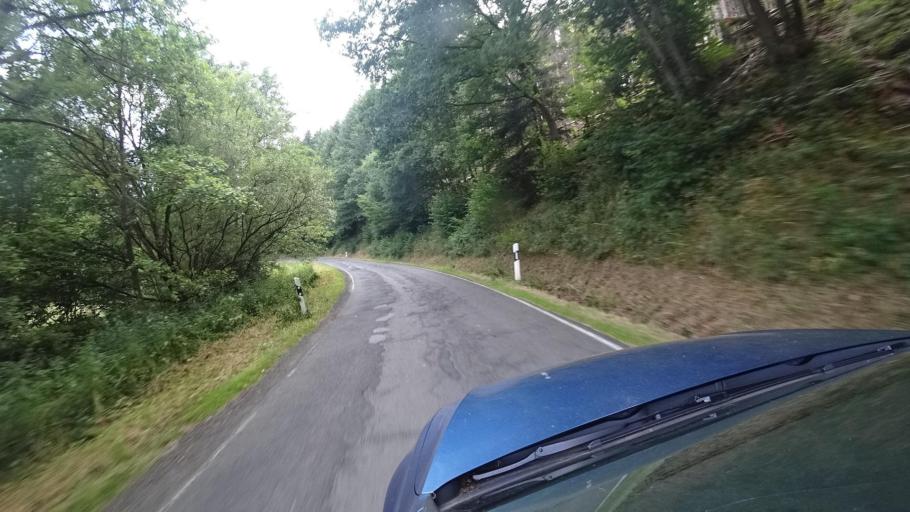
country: DE
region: Rheinland-Pfalz
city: Orfgen
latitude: 50.6621
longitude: 7.5349
